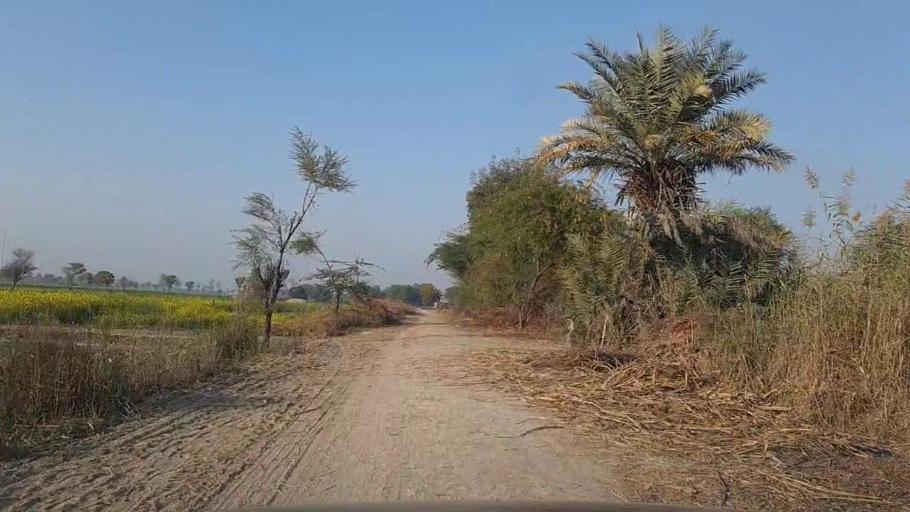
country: PK
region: Sindh
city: Daur
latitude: 26.4637
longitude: 68.4381
